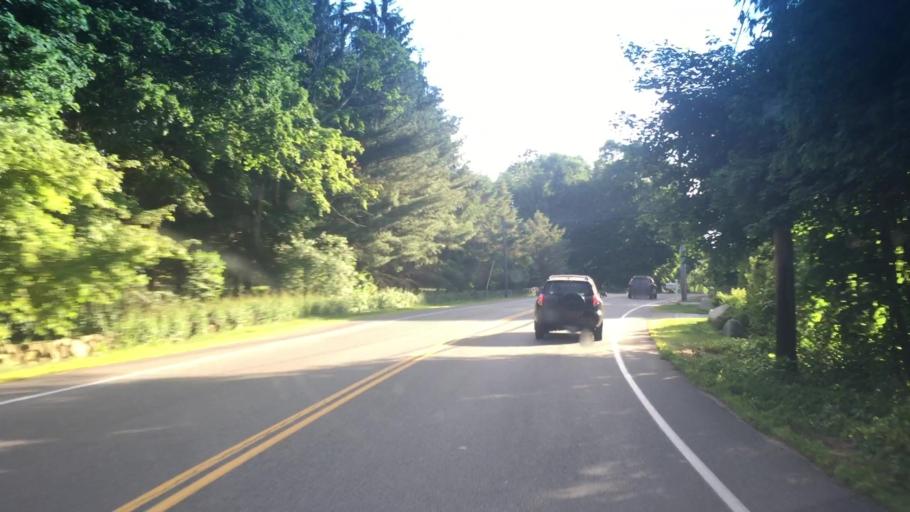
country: US
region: Massachusetts
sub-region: Norfolk County
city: Medfield
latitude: 42.2010
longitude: -71.2676
